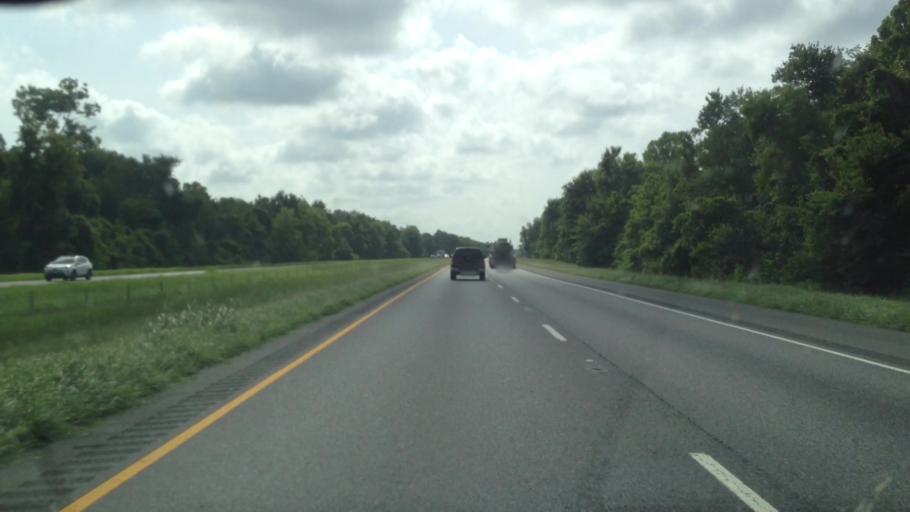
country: US
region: Louisiana
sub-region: Ascension Parish
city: Sorrento
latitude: 30.1488
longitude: -90.7778
